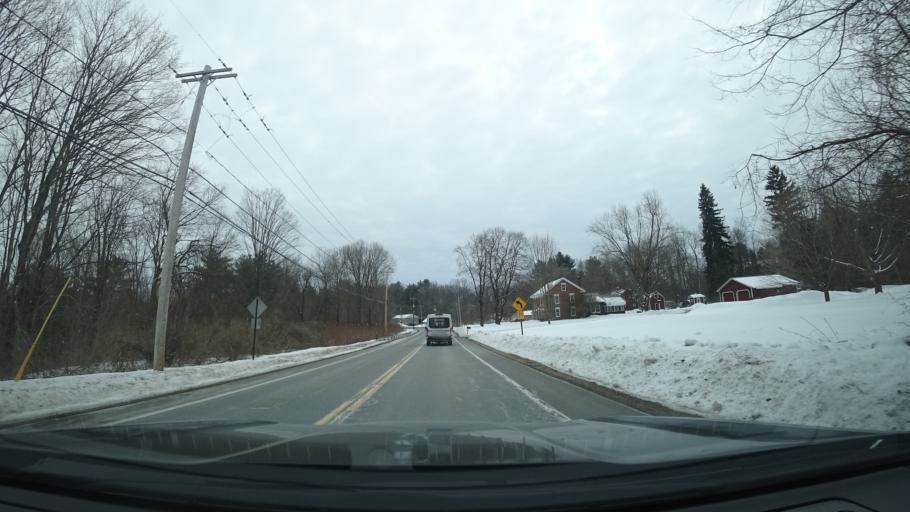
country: US
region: New York
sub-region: Washington County
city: Fort Edward
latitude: 43.2619
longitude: -73.6065
